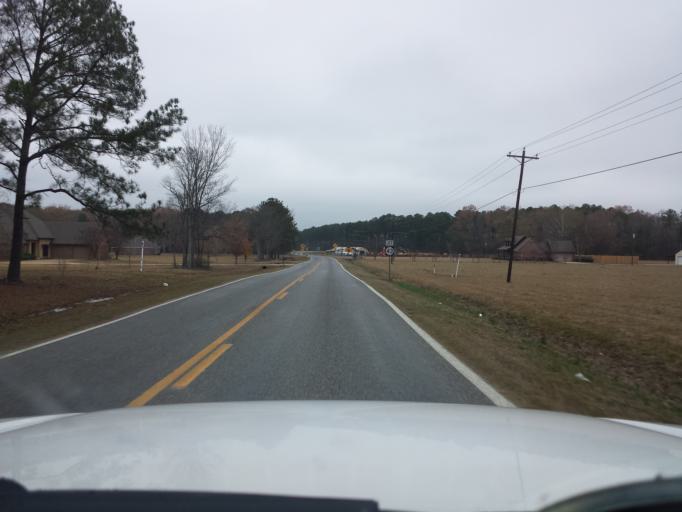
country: US
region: Mississippi
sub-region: Madison County
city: Canton
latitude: 32.4953
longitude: -89.9240
